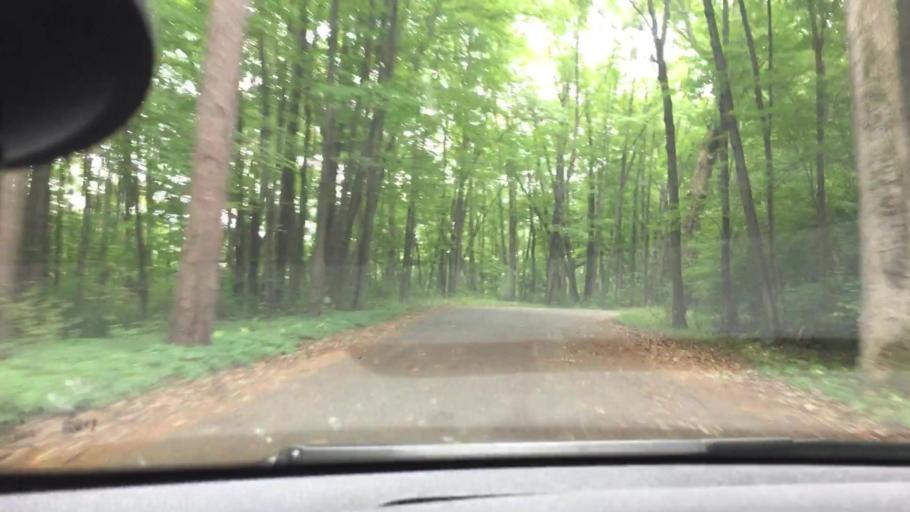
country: US
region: Wisconsin
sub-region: Chippewa County
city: Chippewa Falls
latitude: 44.9633
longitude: -91.4026
